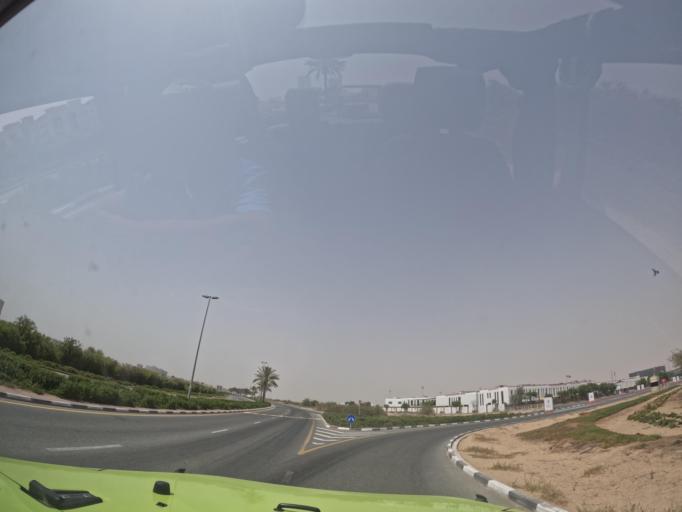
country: AE
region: Dubai
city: Dubai
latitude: 25.1053
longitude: 55.3977
